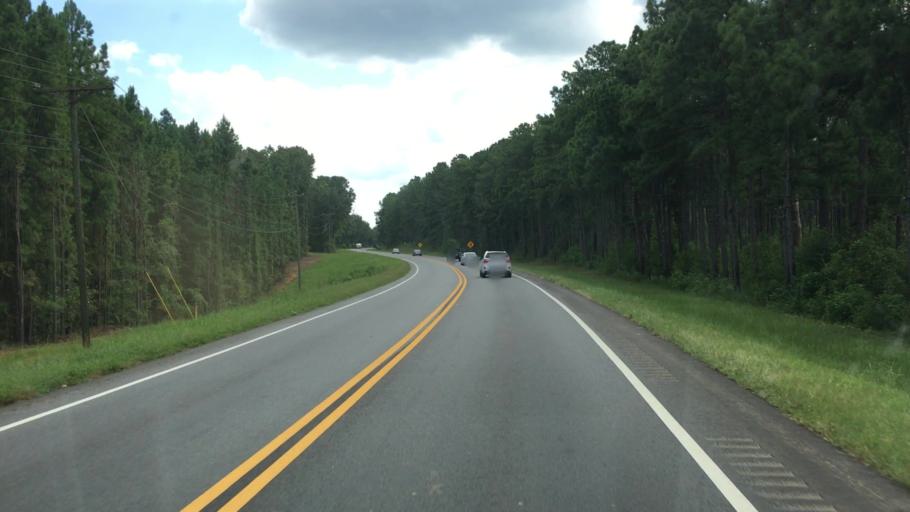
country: US
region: Georgia
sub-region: Putnam County
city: Eatonton
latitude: 33.3998
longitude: -83.3687
